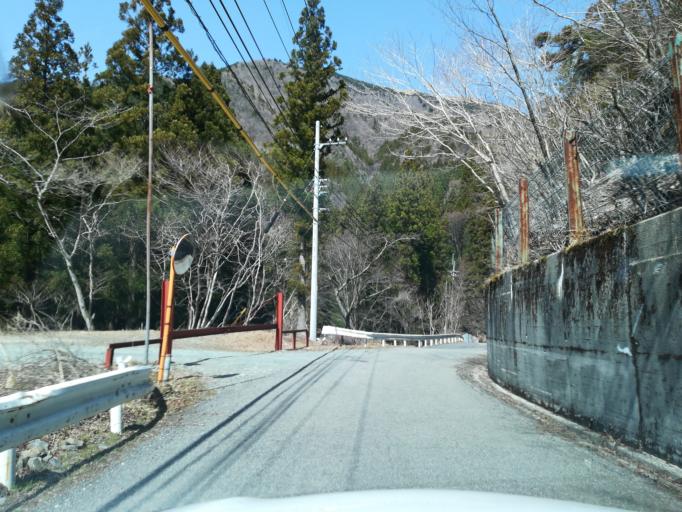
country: JP
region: Tokushima
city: Wakimachi
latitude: 33.8519
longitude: 134.0301
